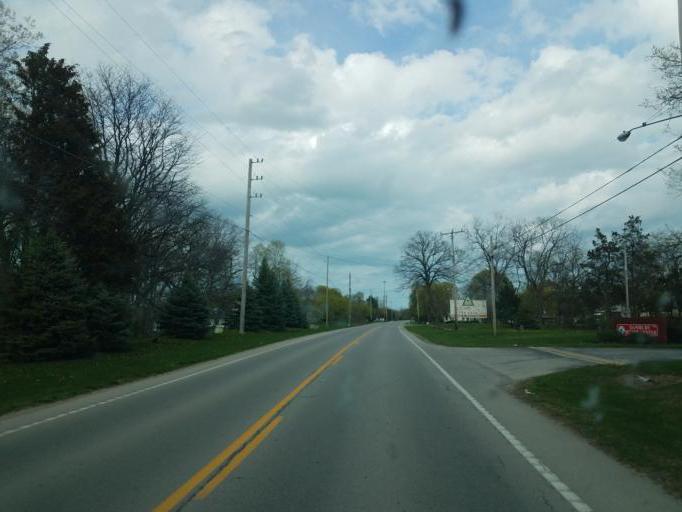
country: US
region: Ohio
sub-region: Erie County
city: Sandusky
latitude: 41.5309
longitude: -82.7736
